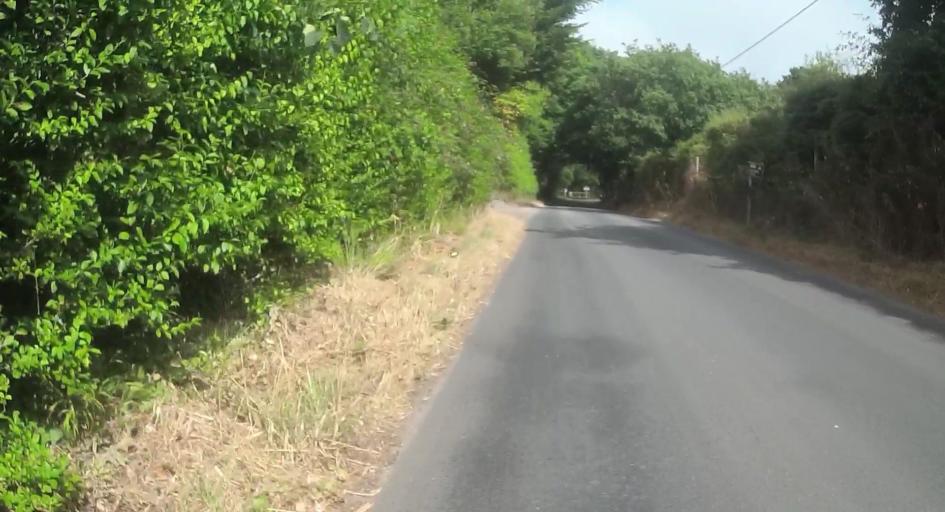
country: GB
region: England
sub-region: Dorset
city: Wool
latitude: 50.6751
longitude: -2.1808
